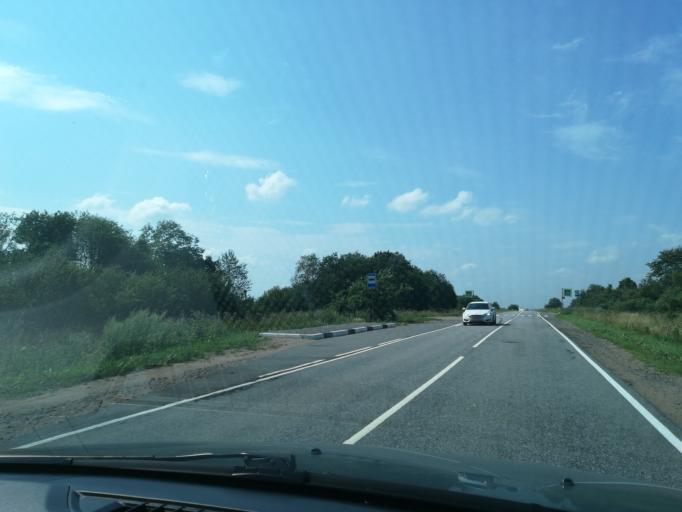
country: RU
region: Leningrad
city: Sista-Palkino
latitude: 59.5770
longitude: 28.7892
